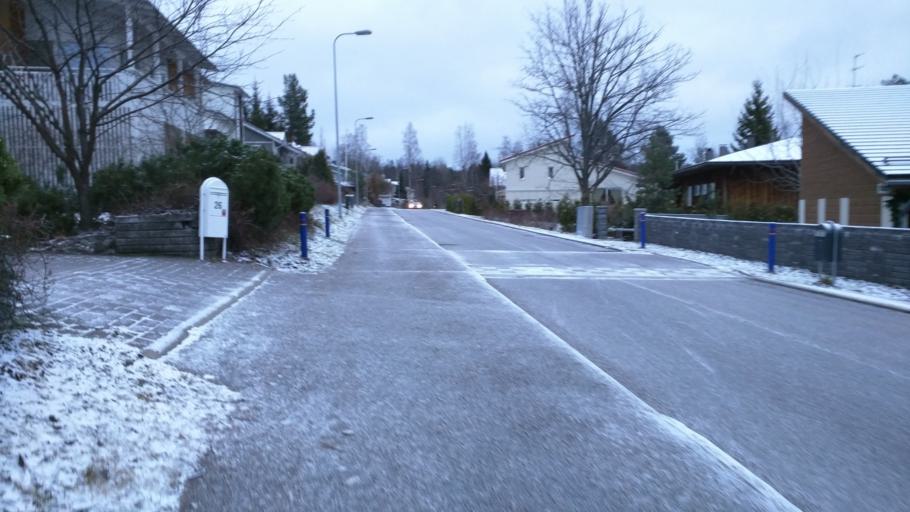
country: FI
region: Uusimaa
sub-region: Helsinki
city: Kilo
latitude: 60.2426
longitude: 24.7776
